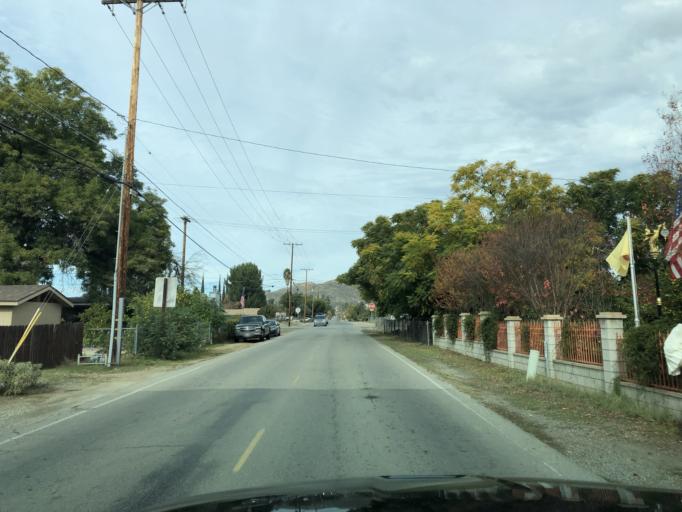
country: US
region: California
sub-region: Riverside County
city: Wildomar
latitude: 33.6189
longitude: -117.2755
